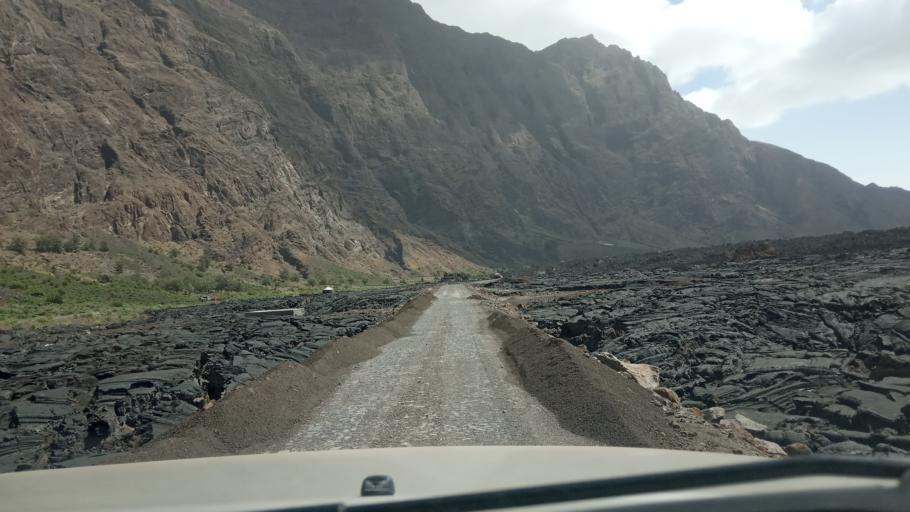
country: CV
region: Mosteiros
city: Porto dos Mosteiros
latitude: 14.9464
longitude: -24.3852
